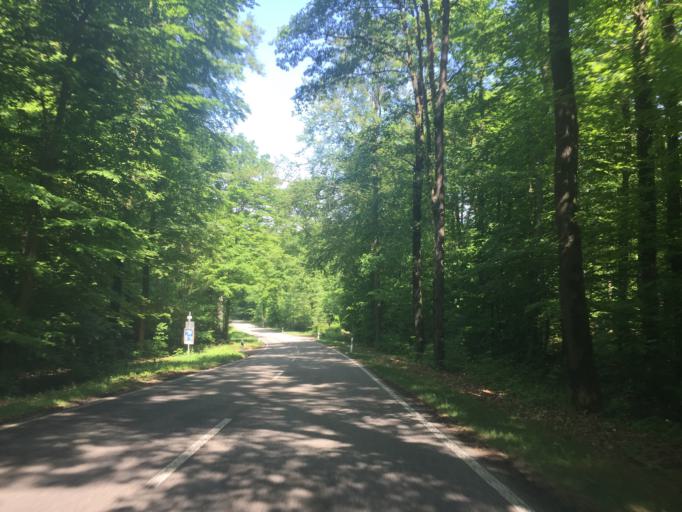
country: DE
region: Baden-Wuerttemberg
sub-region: Karlsruhe Region
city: Malsch
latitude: 48.8671
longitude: 8.3508
